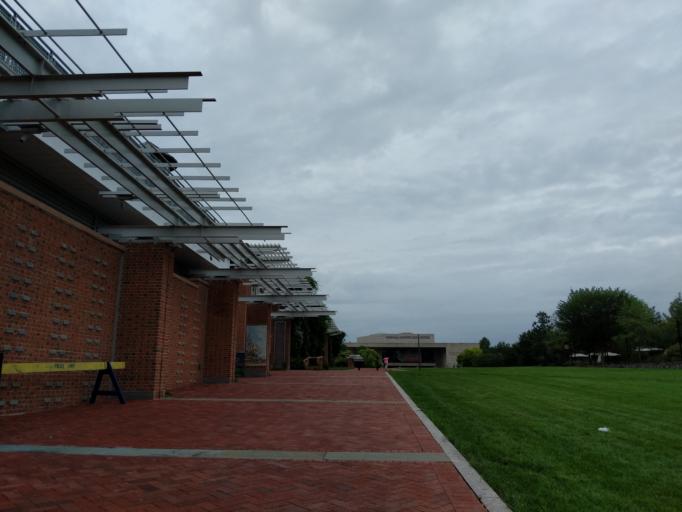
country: US
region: Pennsylvania
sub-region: Philadelphia County
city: Philadelphia
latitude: 39.9510
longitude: -75.1498
